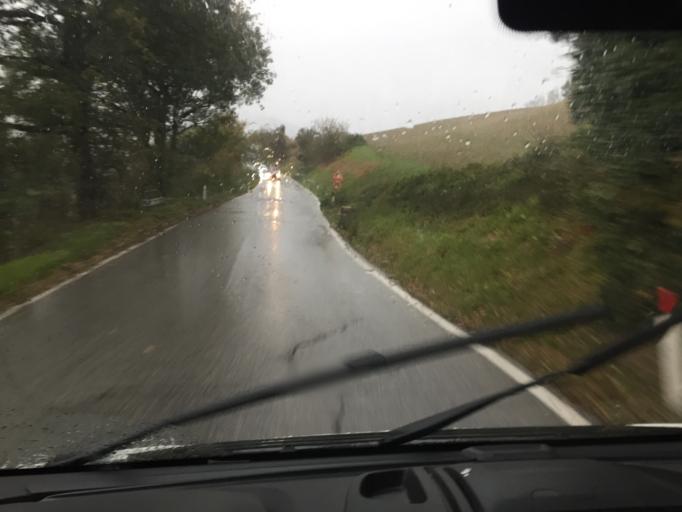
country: IT
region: The Marches
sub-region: Provincia di Macerata
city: Camerino
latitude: 43.1262
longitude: 13.0628
